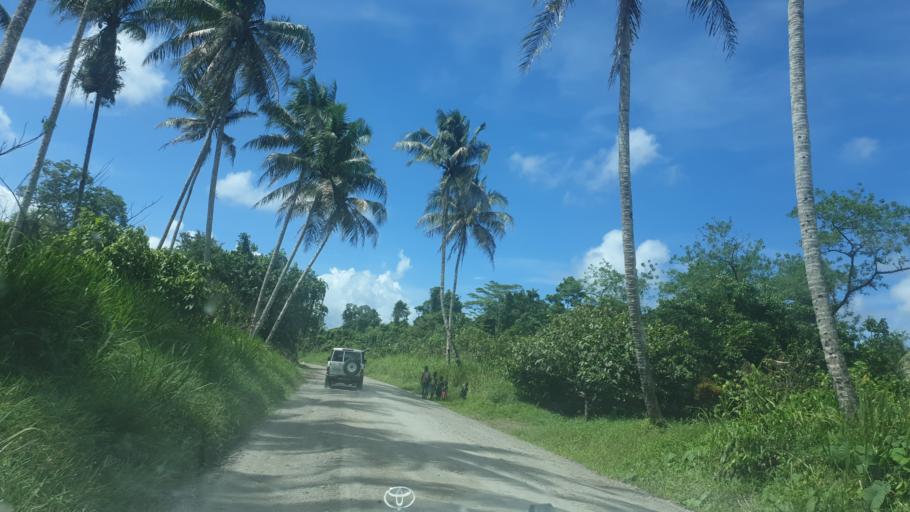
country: PG
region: Bougainville
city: Panguna
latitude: -6.7385
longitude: 155.6652
